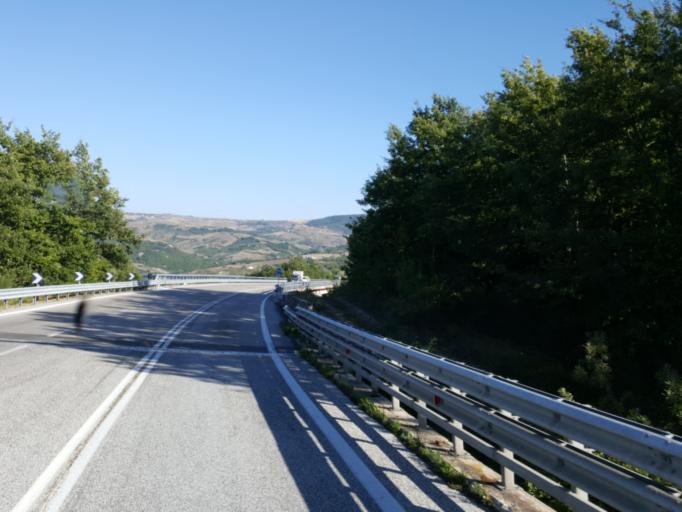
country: IT
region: Molise
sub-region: Provincia di Isernia
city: Bagnoli del Trigno
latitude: 41.7302
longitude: 14.4376
